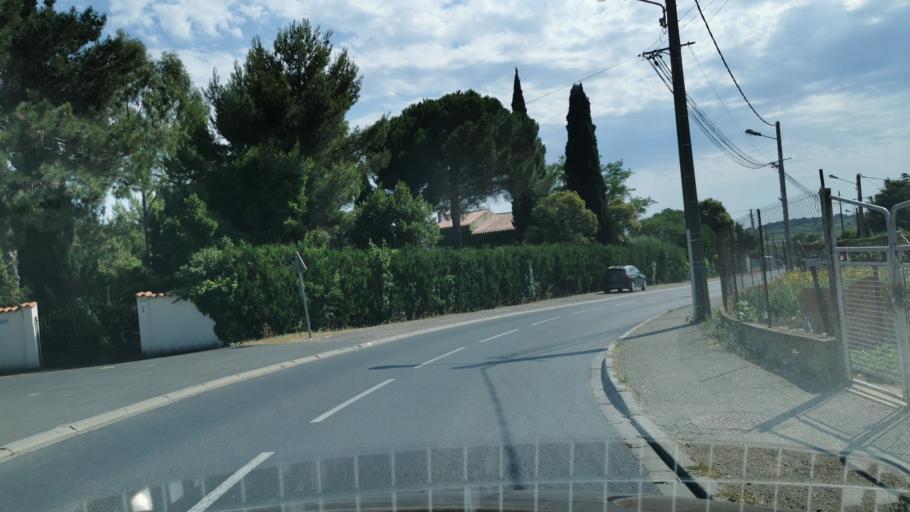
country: FR
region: Languedoc-Roussillon
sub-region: Departement de l'Herault
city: Cazouls-les-Beziers
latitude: 43.3884
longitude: 3.1067
